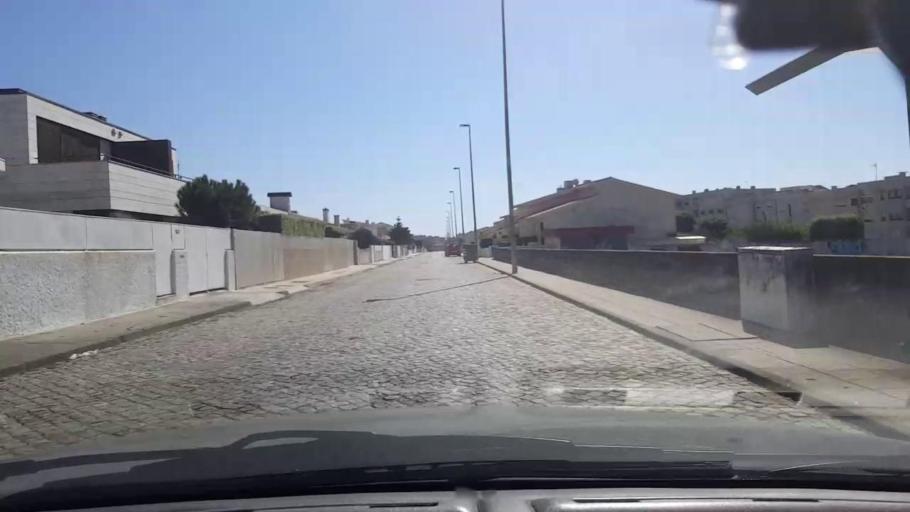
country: PT
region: Porto
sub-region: Vila do Conde
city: Arvore
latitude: 41.3099
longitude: -8.7361
